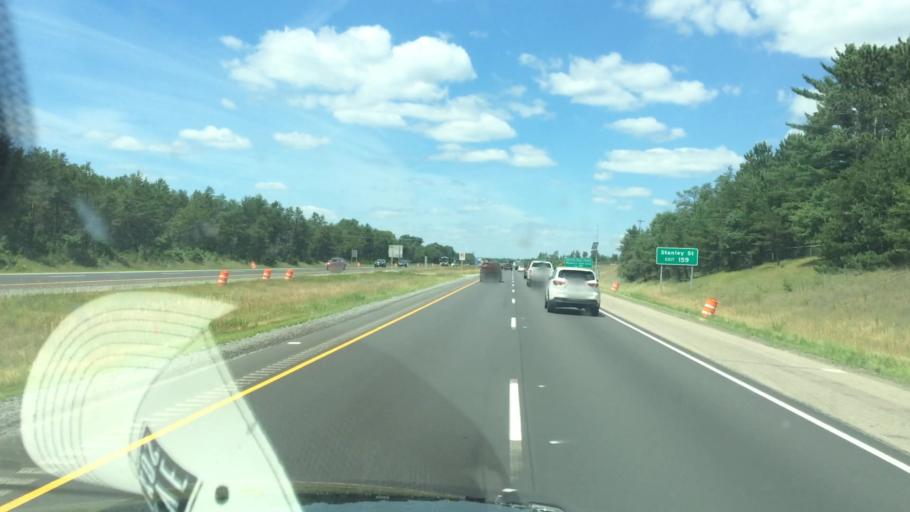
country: US
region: Wisconsin
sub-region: Portage County
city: Stevens Point
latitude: 44.5329
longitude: -89.5366
